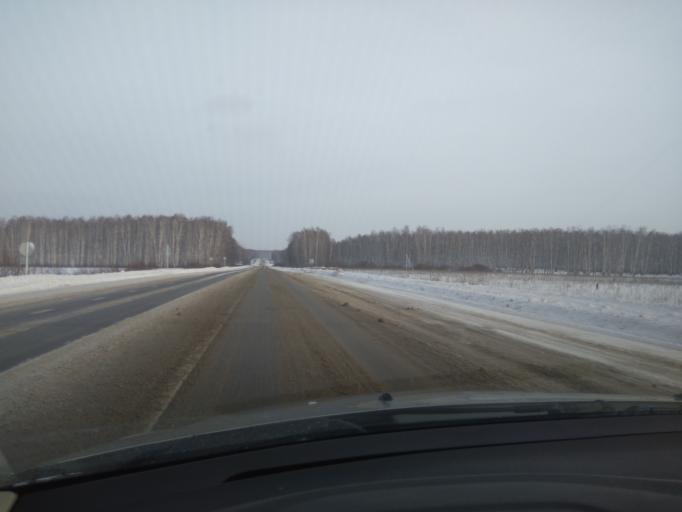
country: RU
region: Sverdlovsk
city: Bogdanovich
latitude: 56.7815
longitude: 61.9971
